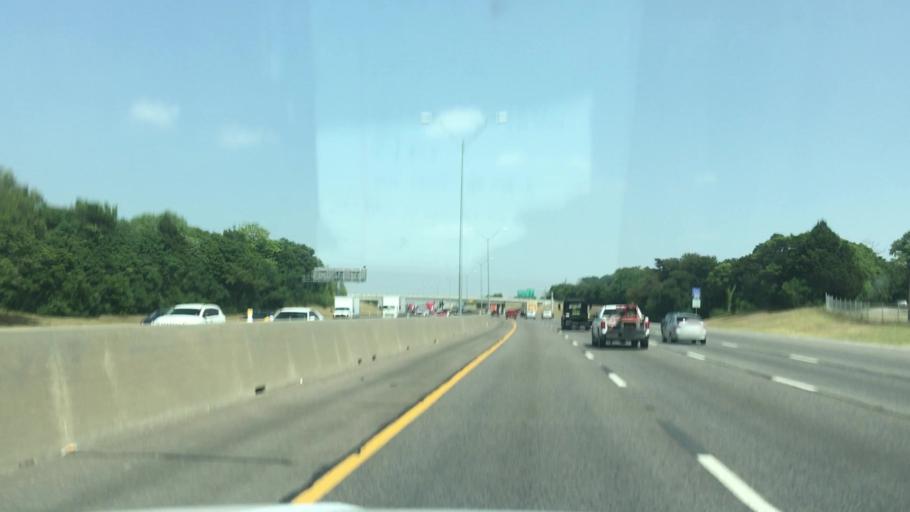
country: US
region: Texas
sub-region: Dallas County
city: Duncanville
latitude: 32.6678
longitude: -96.9204
